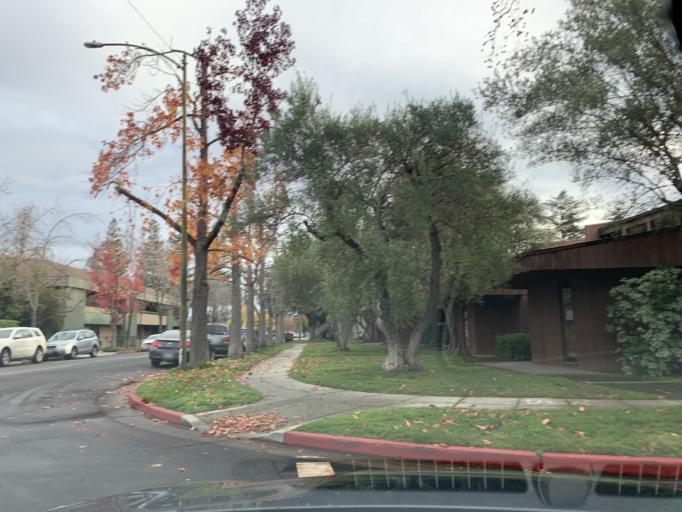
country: US
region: California
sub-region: Santa Clara County
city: Cambrian Park
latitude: 37.2472
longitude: -121.9518
